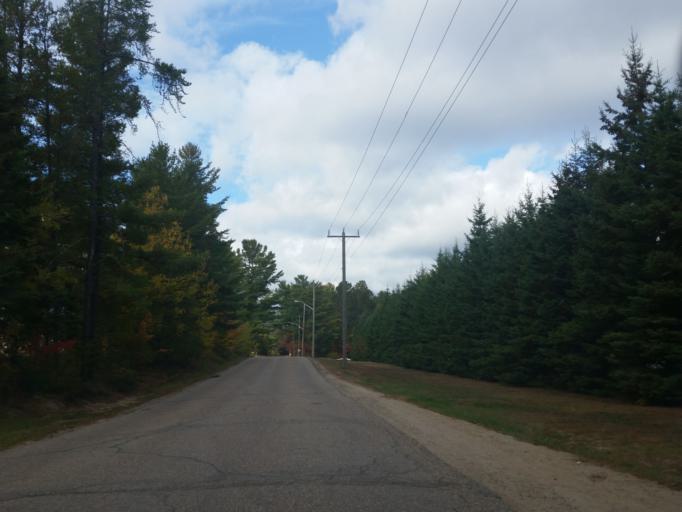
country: CA
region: Ontario
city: Deep River
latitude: 46.0951
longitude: -77.4841
